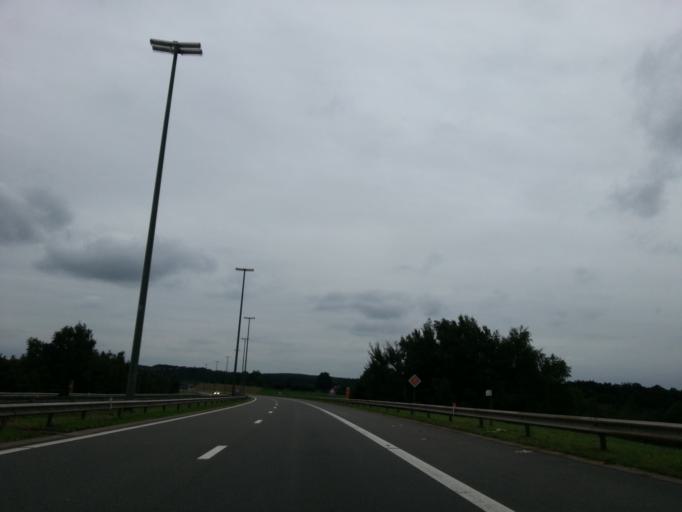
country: BE
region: Wallonia
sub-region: Province de Liege
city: Jalhay
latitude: 50.5206
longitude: 5.9414
